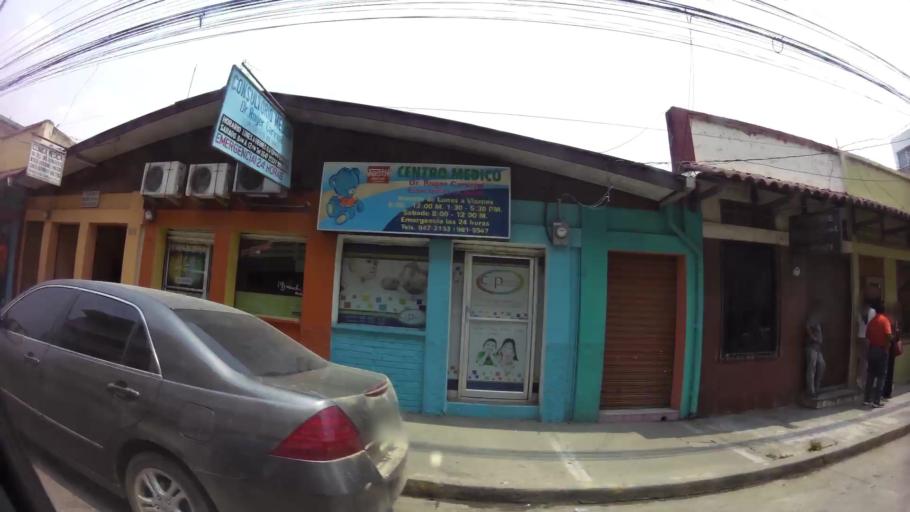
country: HN
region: Yoro
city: El Progreso
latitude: 15.4002
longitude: -87.8104
